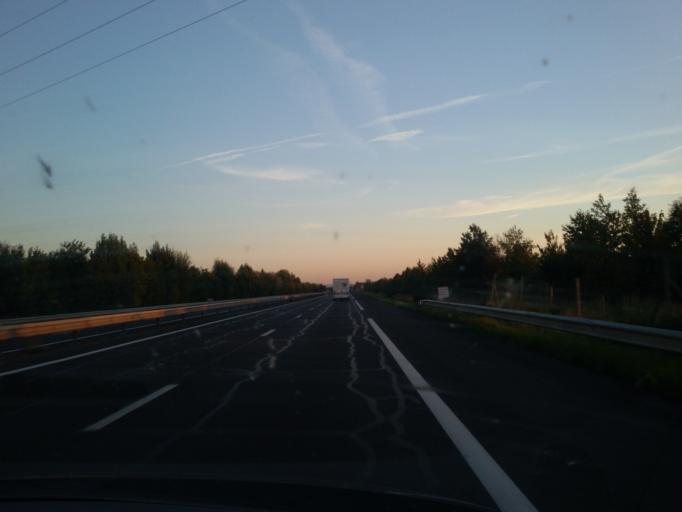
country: FR
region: Auvergne
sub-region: Departement du Puy-de-Dome
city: Menetrol
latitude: 45.8636
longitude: 3.1581
